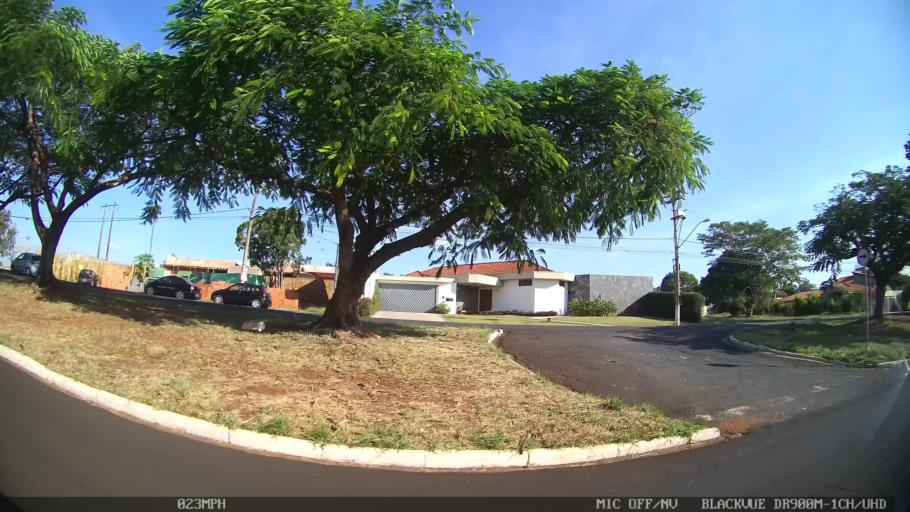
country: BR
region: Sao Paulo
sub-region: Ribeirao Preto
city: Ribeirao Preto
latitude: -21.2026
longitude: -47.7821
